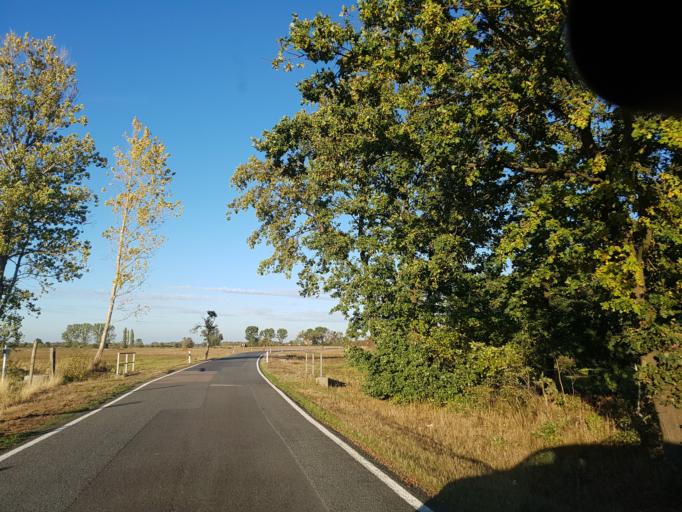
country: DE
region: Brandenburg
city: Muhlberg
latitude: 51.4969
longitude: 13.2679
